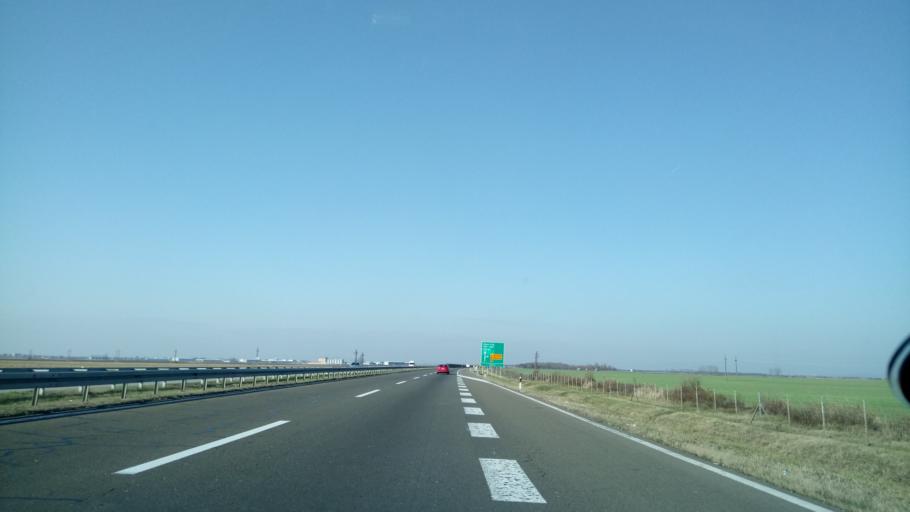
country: RS
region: Autonomna Pokrajina Vojvodina
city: Nova Pazova
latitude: 44.9732
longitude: 20.2302
